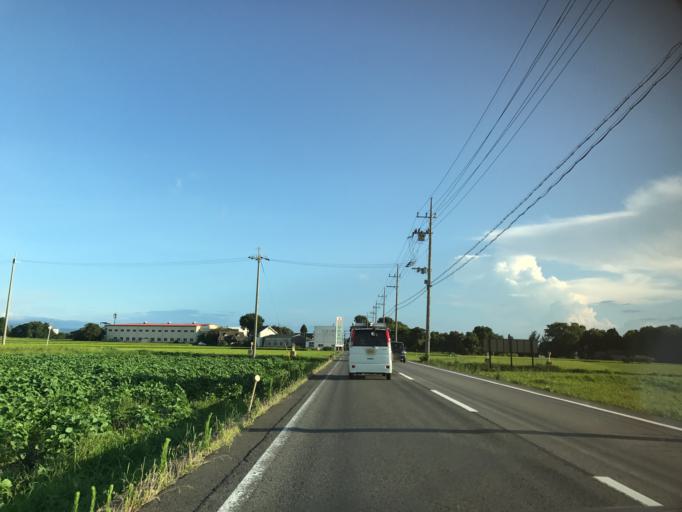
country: JP
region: Shiga Prefecture
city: Youkaichi
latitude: 35.1241
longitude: 136.2574
